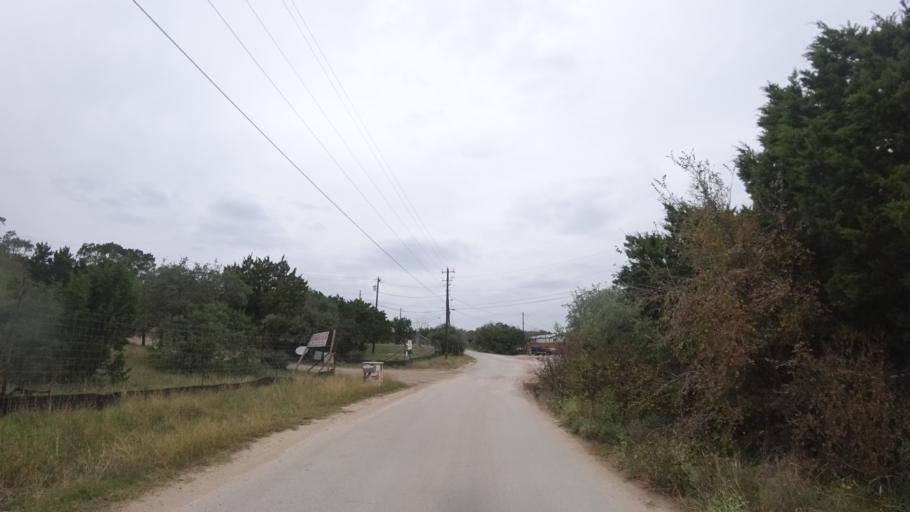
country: US
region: Texas
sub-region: Travis County
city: Hudson Bend
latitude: 30.3838
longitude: -97.9383
